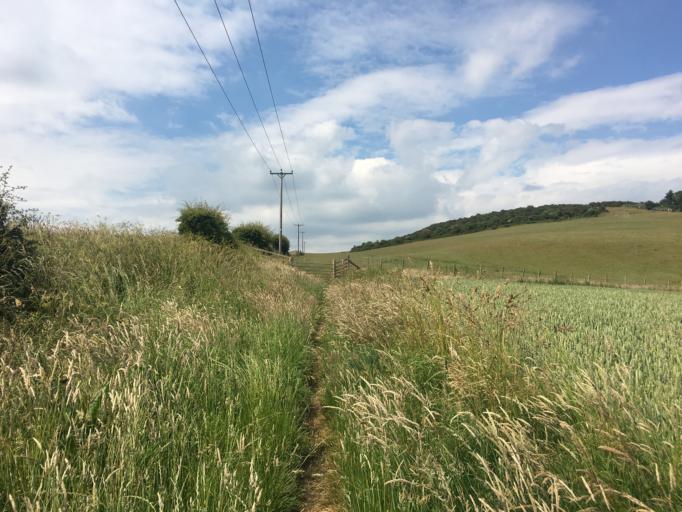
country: GB
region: England
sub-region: Northumberland
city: Belford
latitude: 55.5991
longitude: -1.7826
